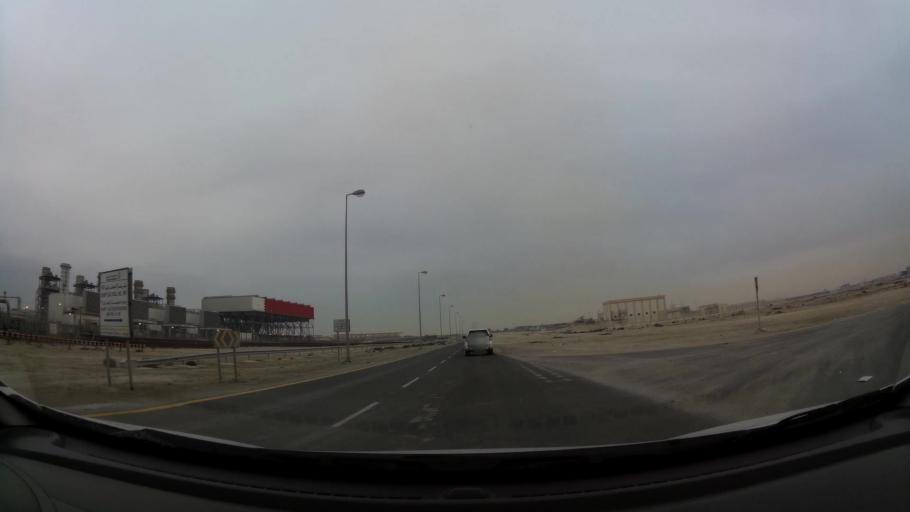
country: BH
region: Northern
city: Ar Rifa'
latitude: 26.0964
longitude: 50.6003
